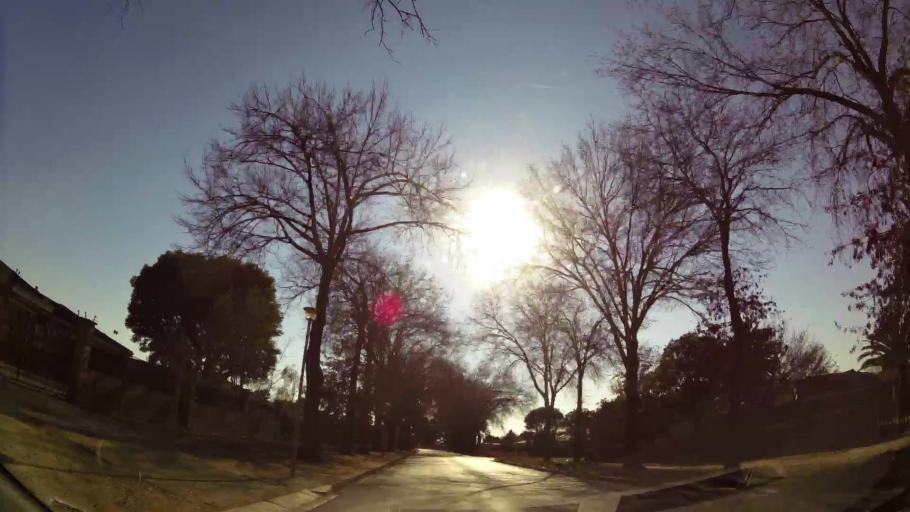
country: ZA
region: Gauteng
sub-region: Ekurhuleni Metropolitan Municipality
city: Benoni
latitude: -26.1603
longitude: 28.3158
